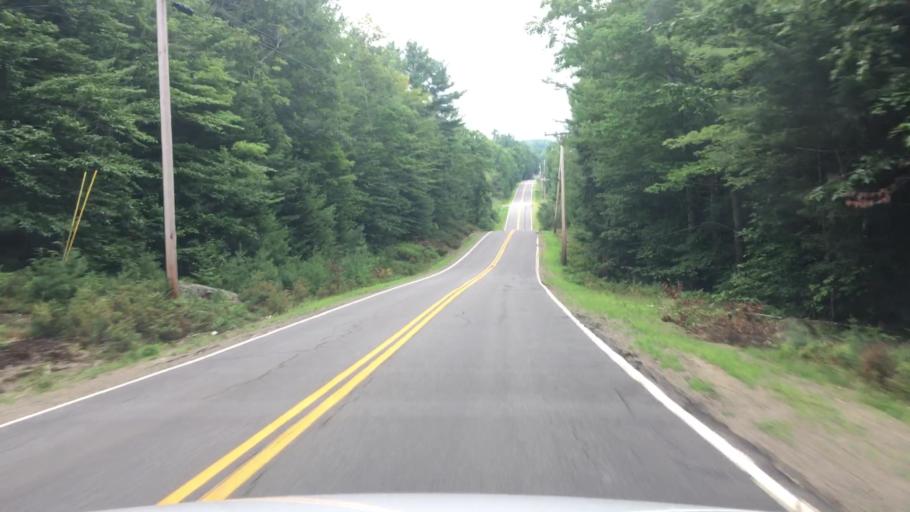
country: US
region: Maine
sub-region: Knox County
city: Washington
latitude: 44.3388
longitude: -69.3435
